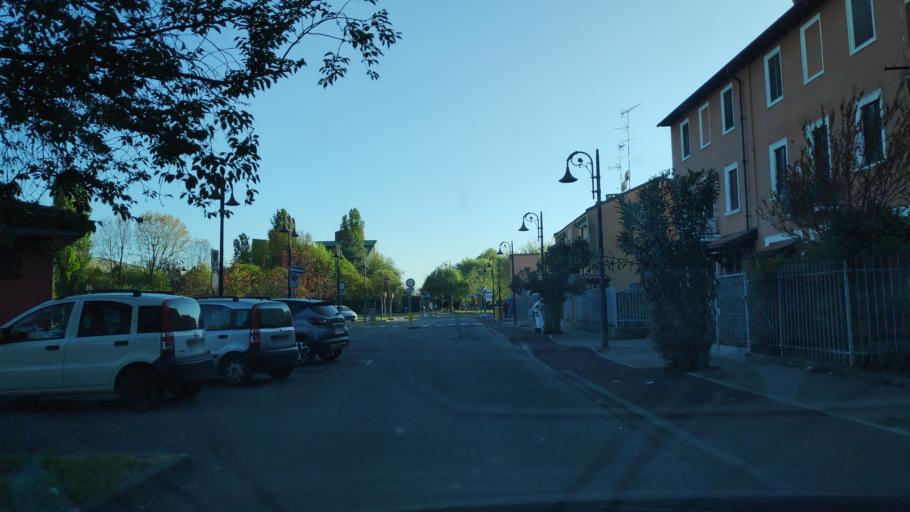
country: IT
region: Lombardy
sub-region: Citta metropolitana di Milano
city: Pieve Emanuele
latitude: 45.3548
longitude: 9.2014
